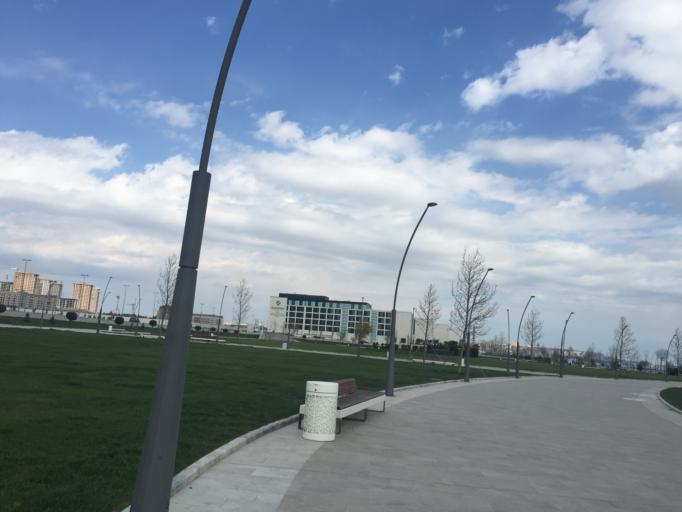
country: AZ
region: Baki
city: Baku
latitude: 40.3752
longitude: 49.8787
